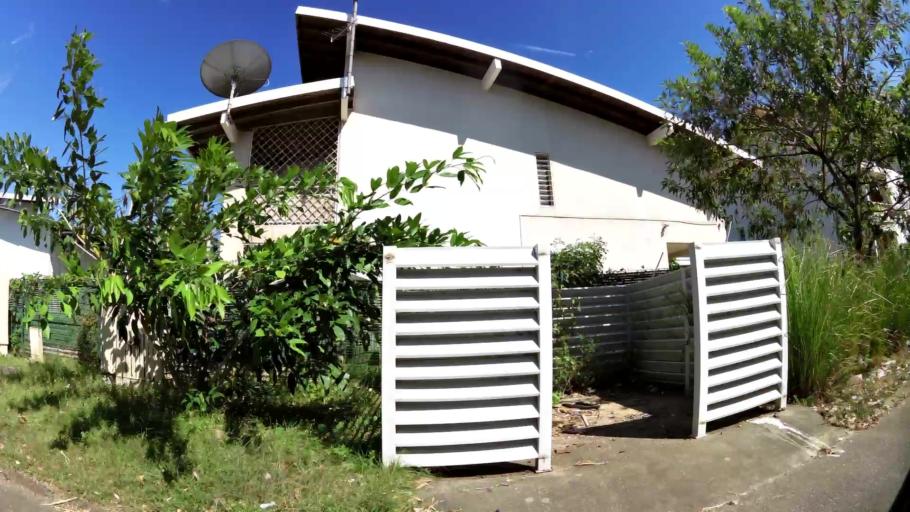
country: GF
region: Guyane
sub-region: Guyane
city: Remire-Montjoly
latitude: 4.9154
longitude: -52.2766
